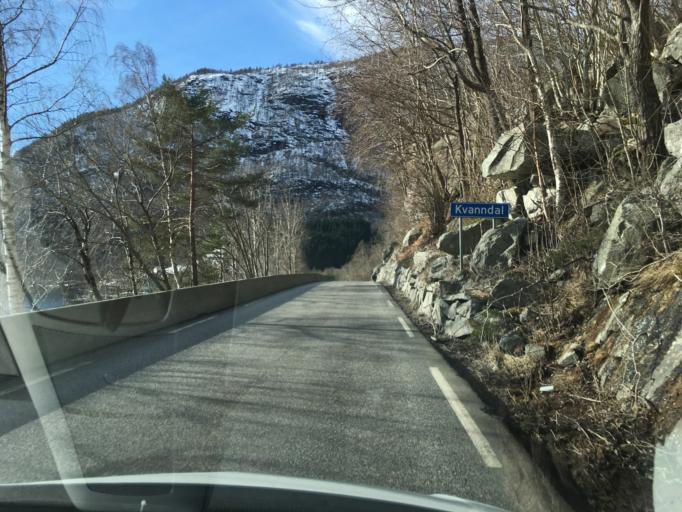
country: NO
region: Hordaland
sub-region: Granvin
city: Granvin
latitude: 60.4740
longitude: 6.6168
